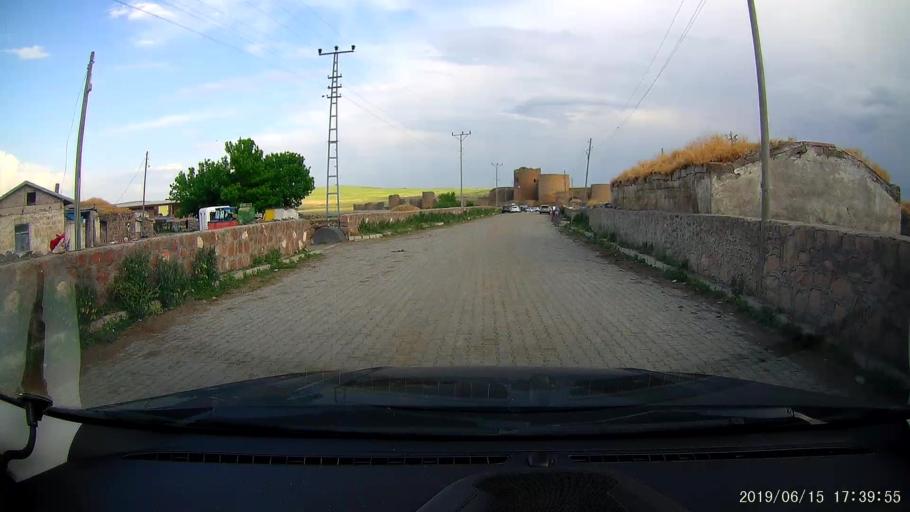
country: TR
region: Kars
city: Basgedikler
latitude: 40.5137
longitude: 43.5717
